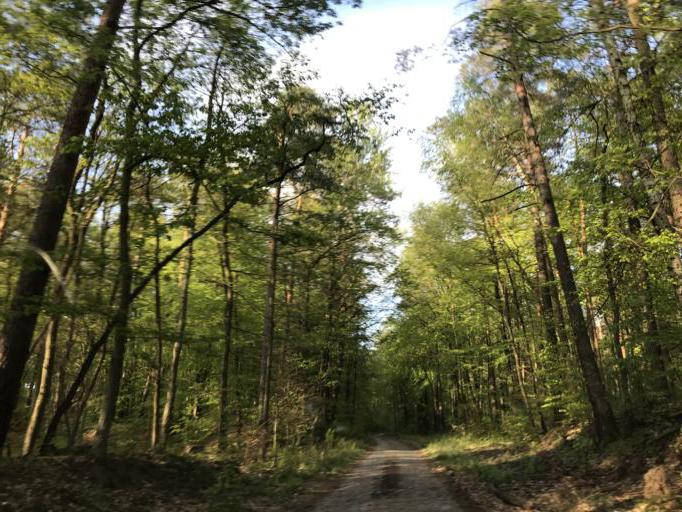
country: DE
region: Brandenburg
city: Joachimsthal
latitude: 52.9689
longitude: 13.7224
